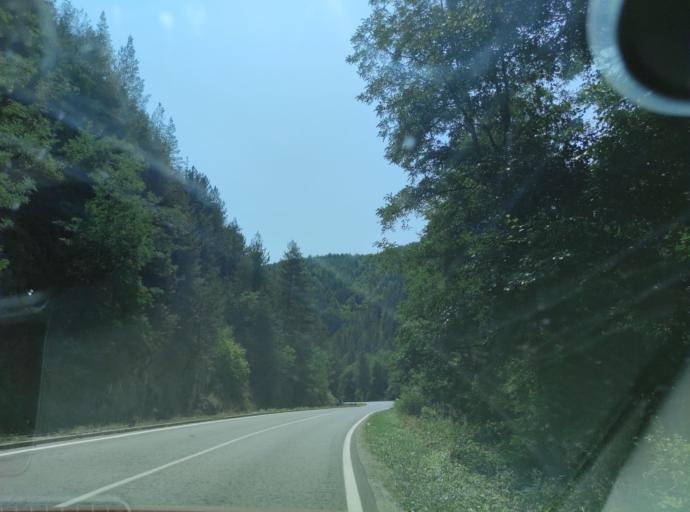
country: BG
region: Blagoevgrad
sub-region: Obshtina Belitsa
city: Belitsa
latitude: 41.8879
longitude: 23.5654
